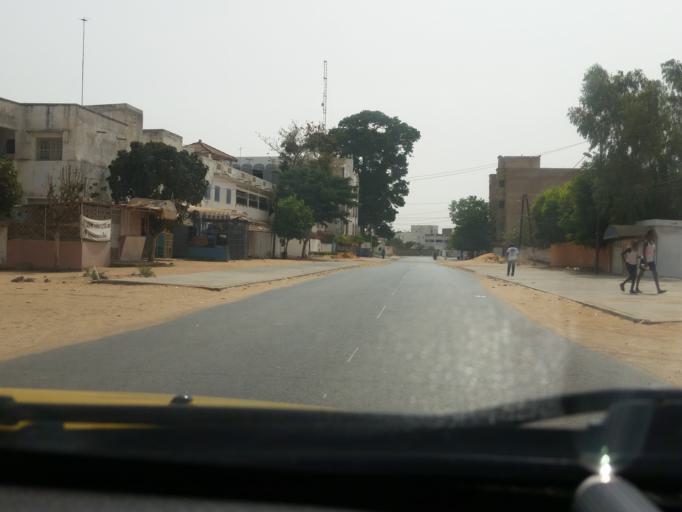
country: SN
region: Thies
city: Thies Nones
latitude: 14.7898
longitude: -16.9338
